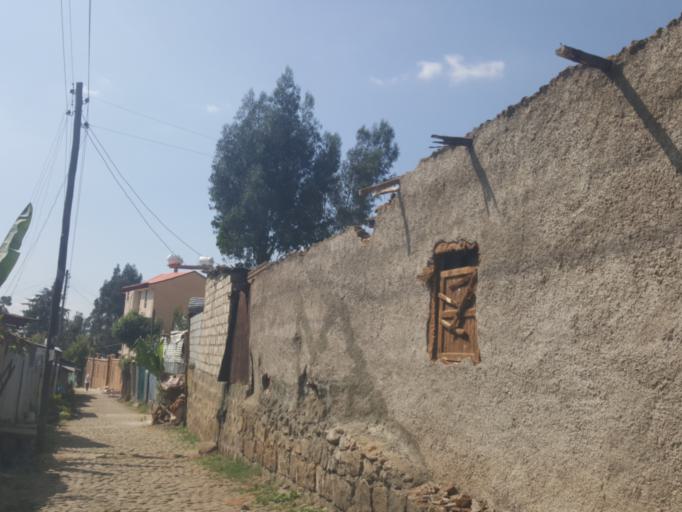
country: ET
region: Adis Abeba
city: Addis Ababa
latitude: 9.0537
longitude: 38.7324
